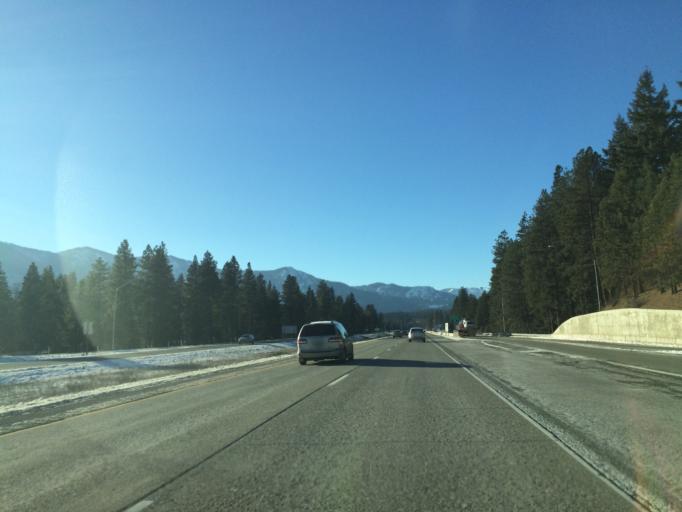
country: US
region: Washington
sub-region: Kittitas County
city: Cle Elum
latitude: 47.1837
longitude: -121.0171
